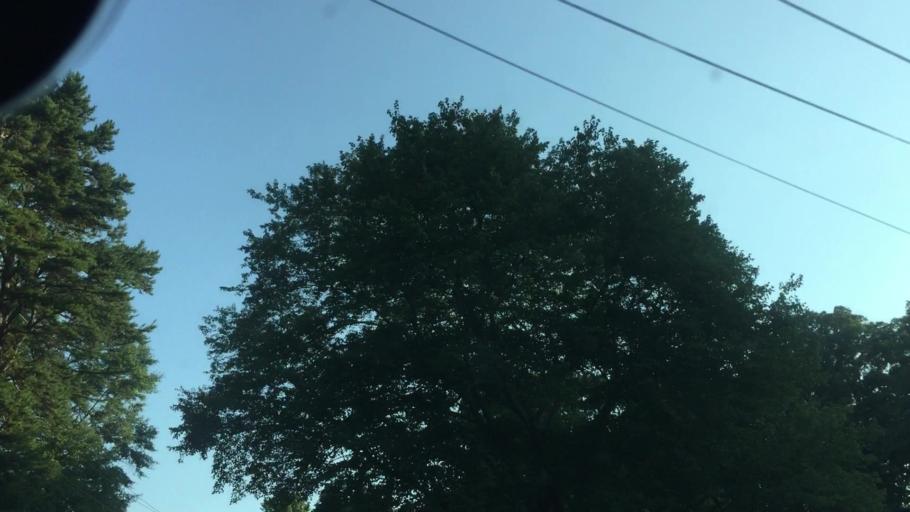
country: US
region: Georgia
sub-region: DeKalb County
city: Panthersville
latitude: 33.7073
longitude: -84.2144
